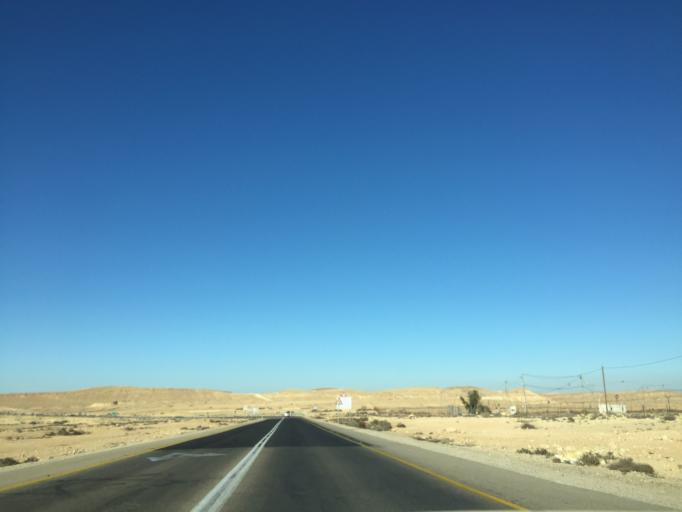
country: IL
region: Southern District
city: Mitzpe Ramon
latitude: 30.6531
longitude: 34.8103
